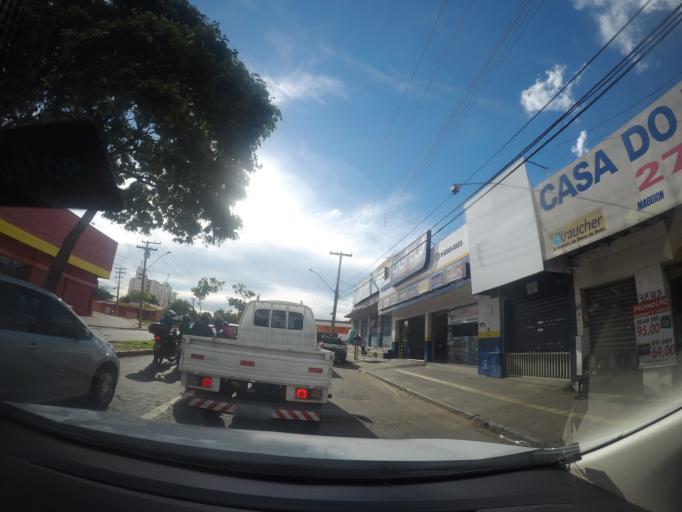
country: BR
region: Goias
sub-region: Goiania
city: Goiania
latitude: -16.6722
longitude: -49.3030
